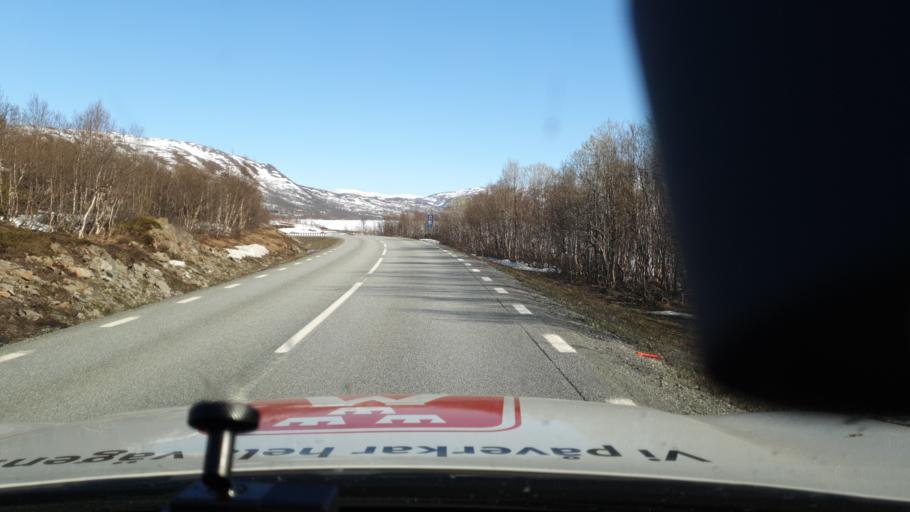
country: NO
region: Nordland
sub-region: Rana
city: Mo i Rana
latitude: 66.1030
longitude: 14.8220
